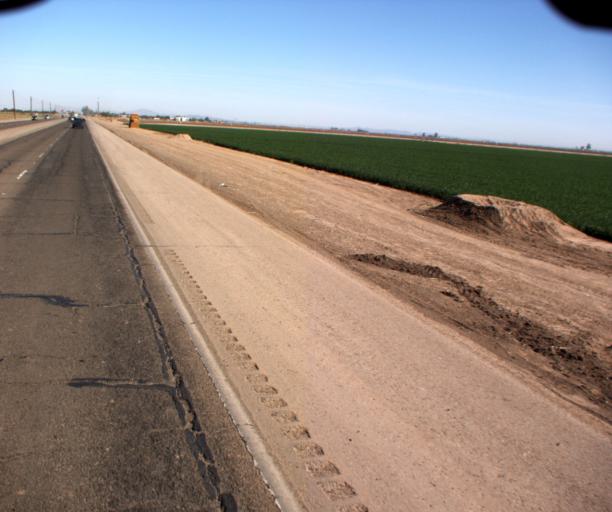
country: US
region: Arizona
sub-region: Yuma County
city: San Luis
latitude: 32.5349
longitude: -114.7868
